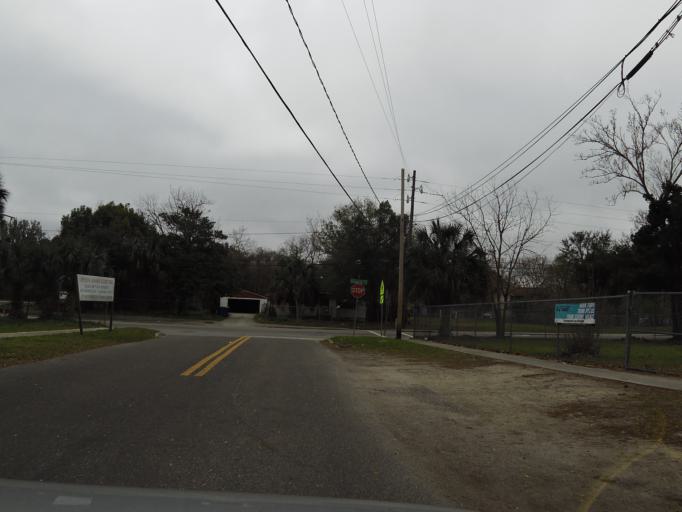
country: US
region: Florida
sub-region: Duval County
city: Jacksonville
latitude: 30.3775
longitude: -81.6995
